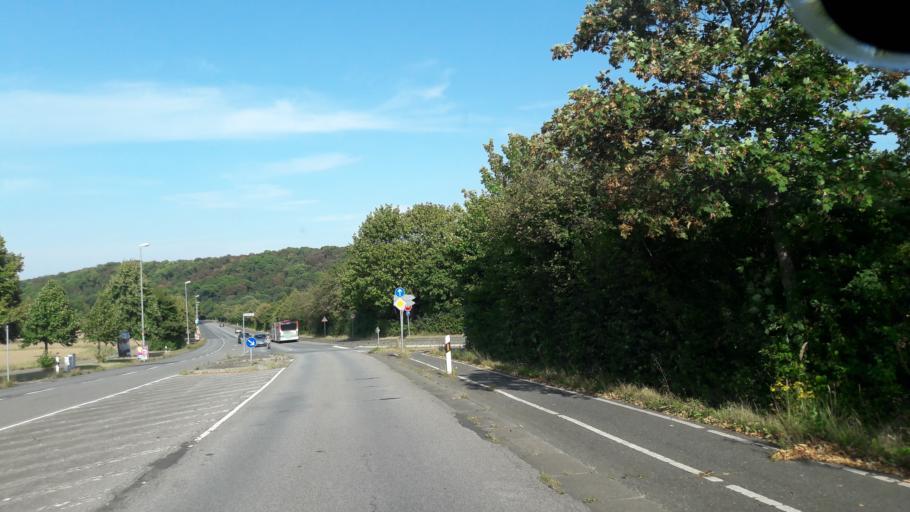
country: DE
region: Lower Saxony
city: Diekholzen
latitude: 52.1282
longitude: 9.9217
